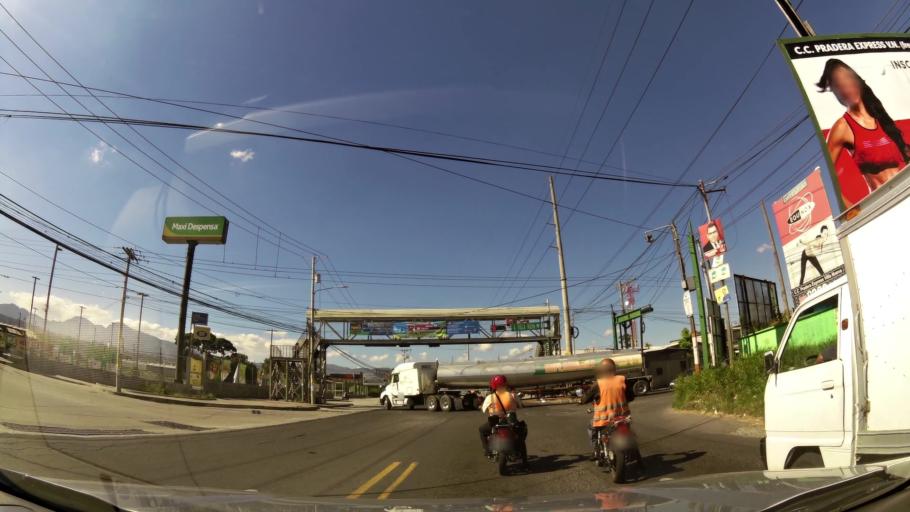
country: GT
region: Guatemala
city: Petapa
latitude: 14.5086
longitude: -90.5699
